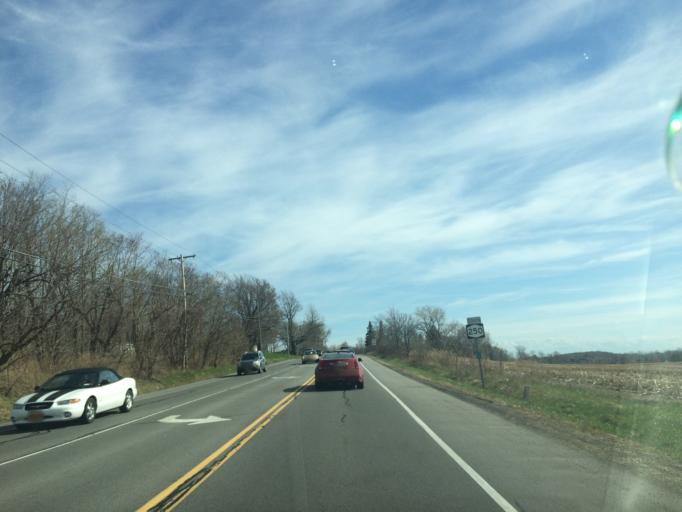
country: US
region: New York
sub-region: Monroe County
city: Webster
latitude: 43.1599
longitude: -77.4316
